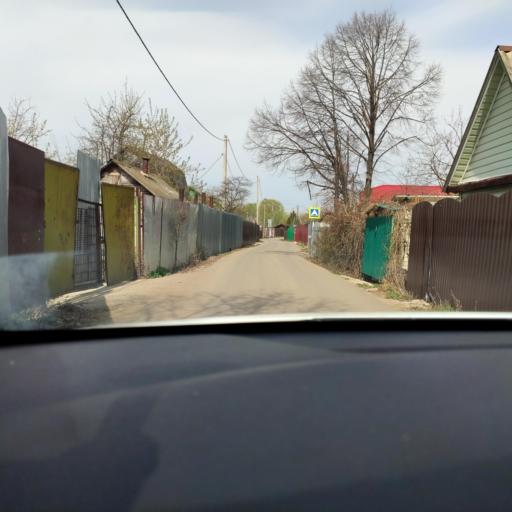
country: RU
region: Tatarstan
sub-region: Gorod Kazan'
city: Kazan
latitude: 55.8531
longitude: 49.1673
